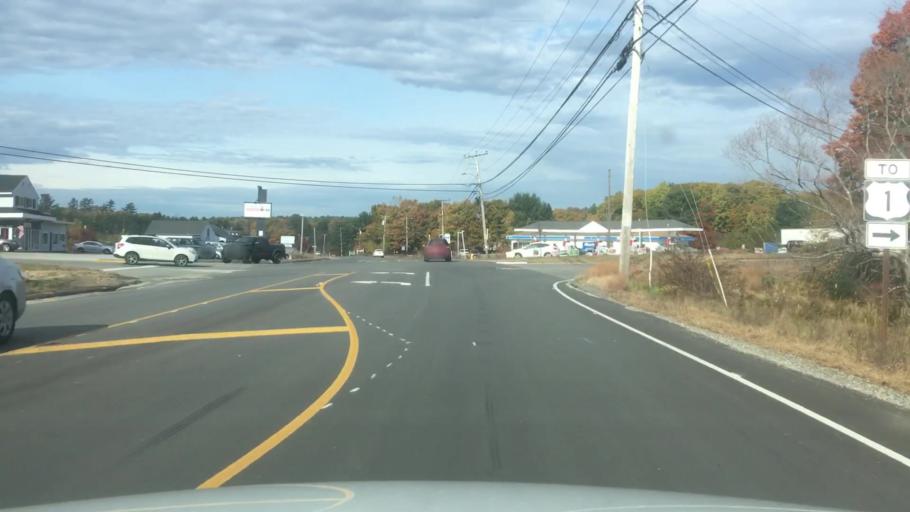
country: US
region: Maine
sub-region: Sagadahoc County
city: Bath
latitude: 43.9092
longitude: -69.8650
